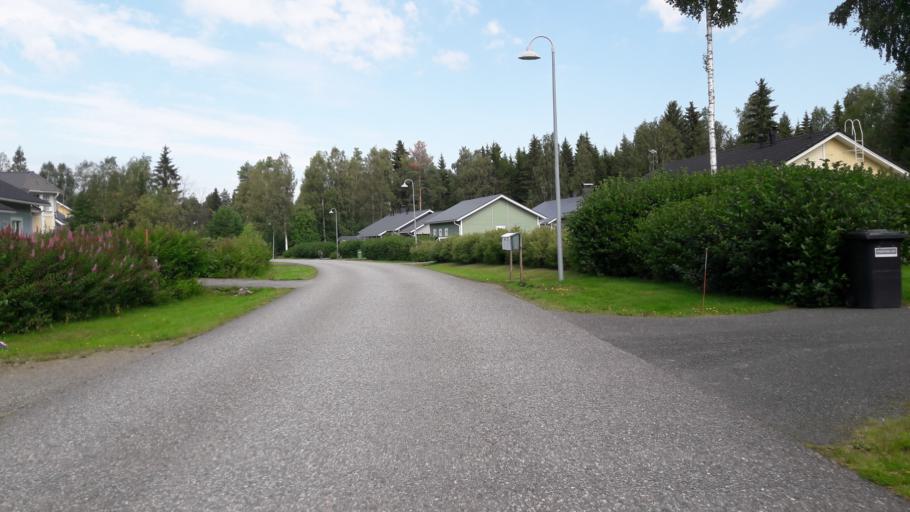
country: FI
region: North Karelia
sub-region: Joensuu
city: Joensuu
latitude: 62.5084
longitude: 29.8308
